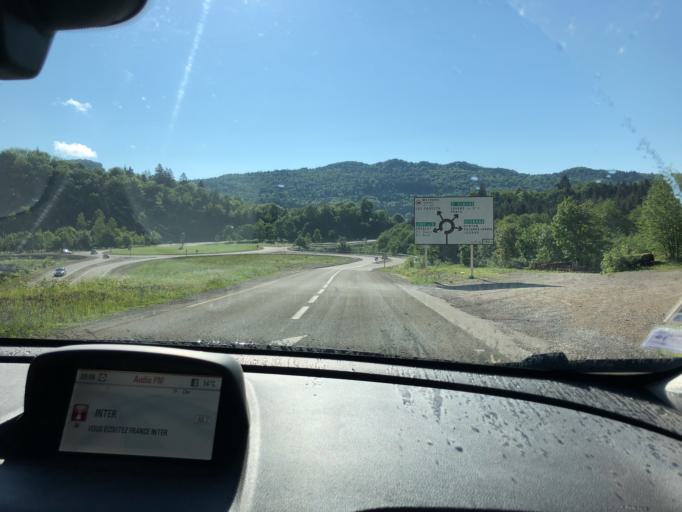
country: FR
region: Franche-Comte
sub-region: Departement du Jura
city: Moirans-en-Montagne
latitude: 46.4132
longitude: 5.7207
